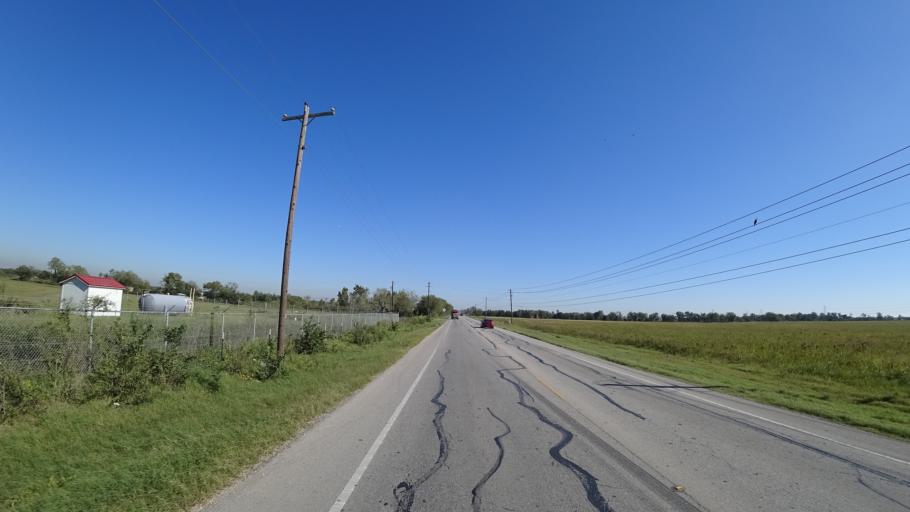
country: US
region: Texas
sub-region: Travis County
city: Hornsby Bend
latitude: 30.2364
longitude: -97.6250
